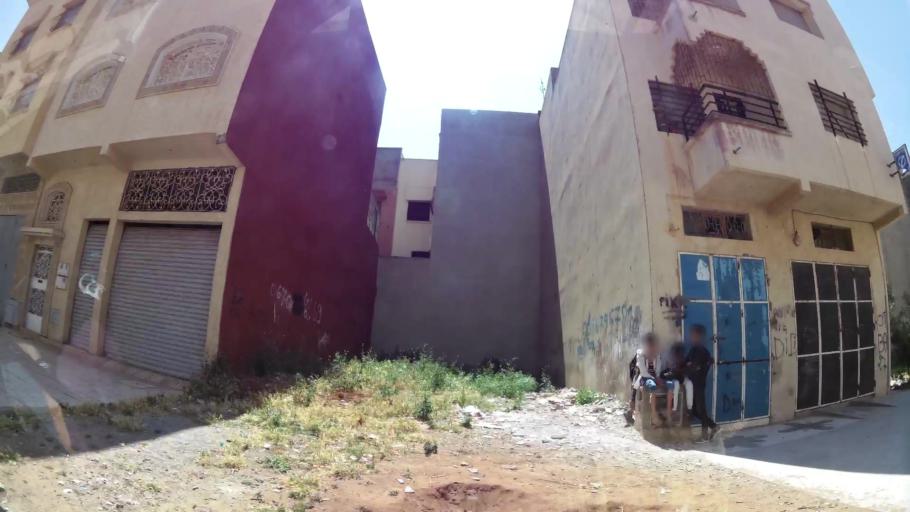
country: MA
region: Rabat-Sale-Zemmour-Zaer
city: Sale
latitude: 34.0788
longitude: -6.7883
